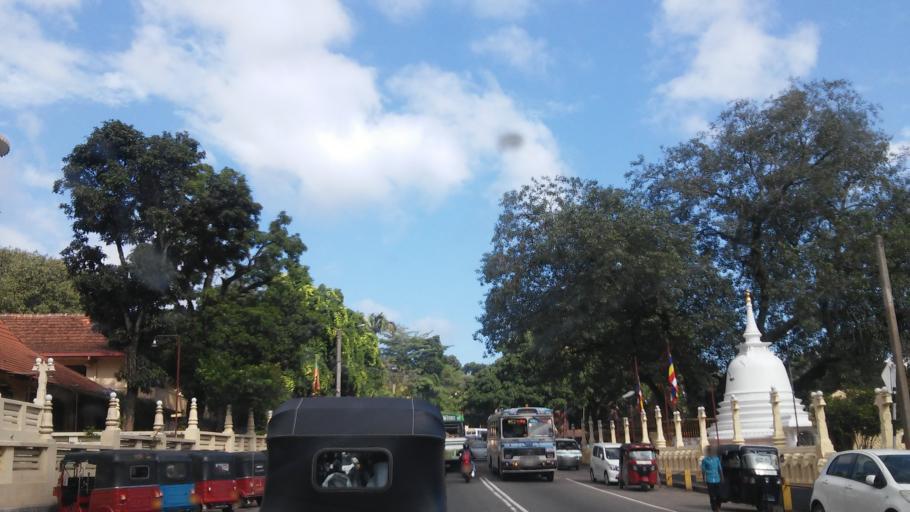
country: LK
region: Central
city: Kandy
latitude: 7.2675
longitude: 80.6011
